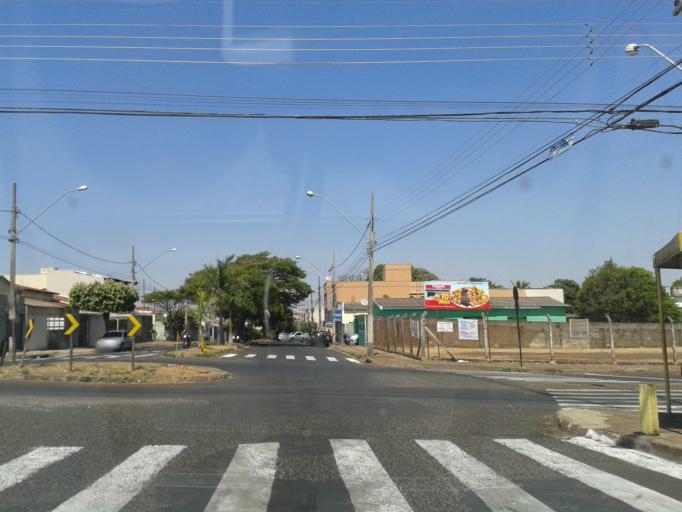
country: BR
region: Minas Gerais
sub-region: Uberlandia
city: Uberlandia
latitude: -18.9020
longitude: -48.2458
